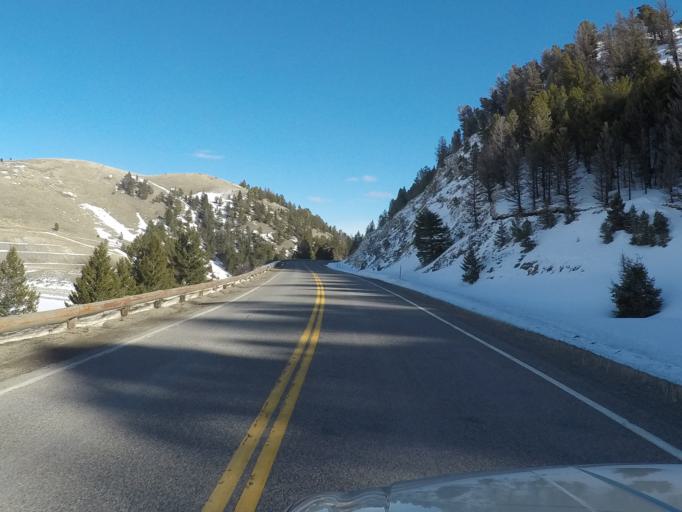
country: US
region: Montana
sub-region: Meagher County
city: White Sulphur Springs
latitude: 46.5790
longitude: -110.5622
